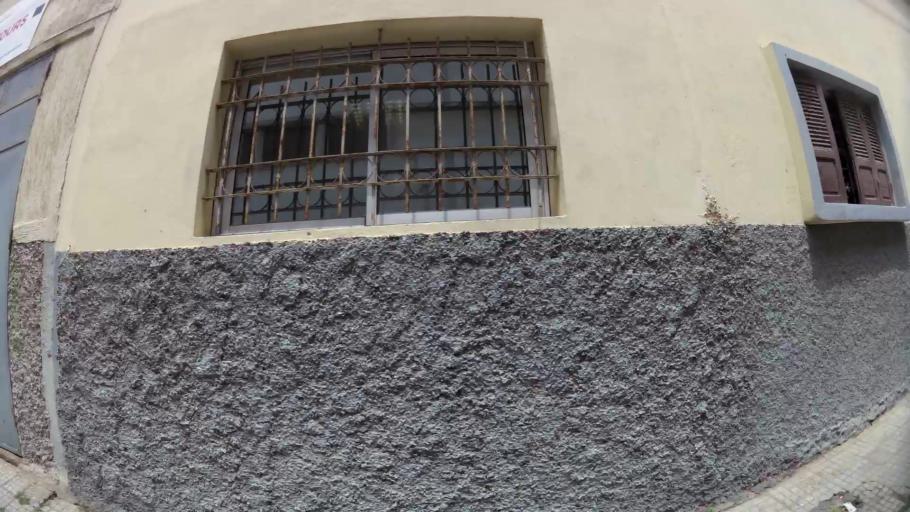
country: MA
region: Rabat-Sale-Zemmour-Zaer
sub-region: Rabat
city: Rabat
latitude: 33.9887
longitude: -6.8814
